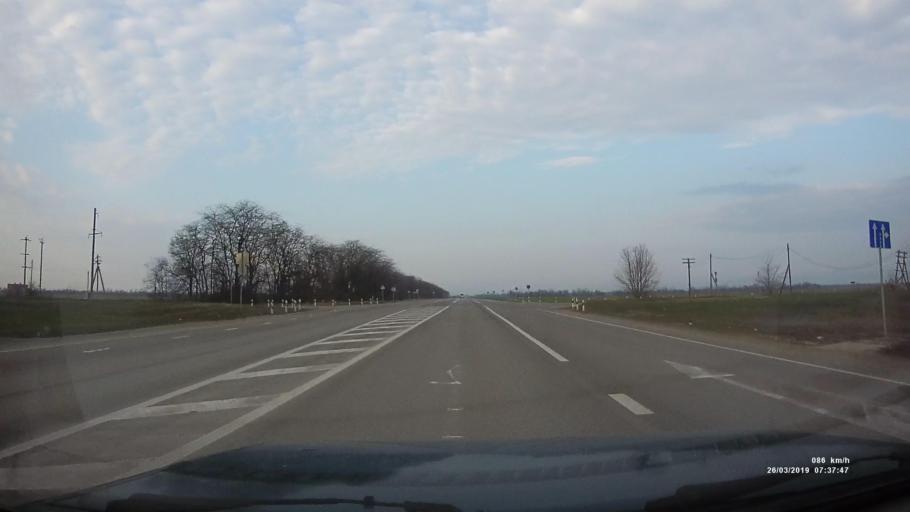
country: RU
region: Rostov
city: Novobessergenovka
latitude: 47.2014
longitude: 38.6950
